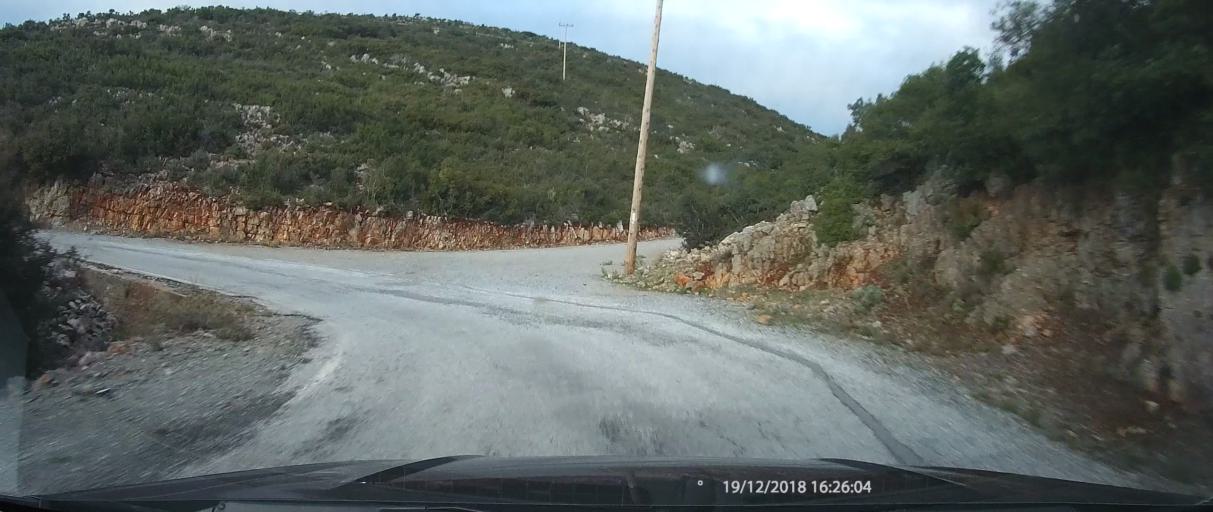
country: GR
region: Peloponnese
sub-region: Nomos Lakonias
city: Kato Glikovrisi
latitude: 36.9577
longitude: 22.8520
